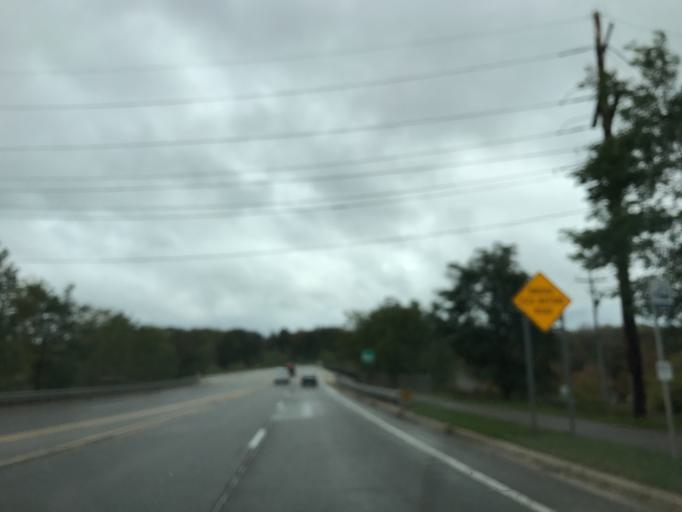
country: US
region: Michigan
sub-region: Washtenaw County
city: Ypsilanti
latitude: 42.2724
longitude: -83.6709
